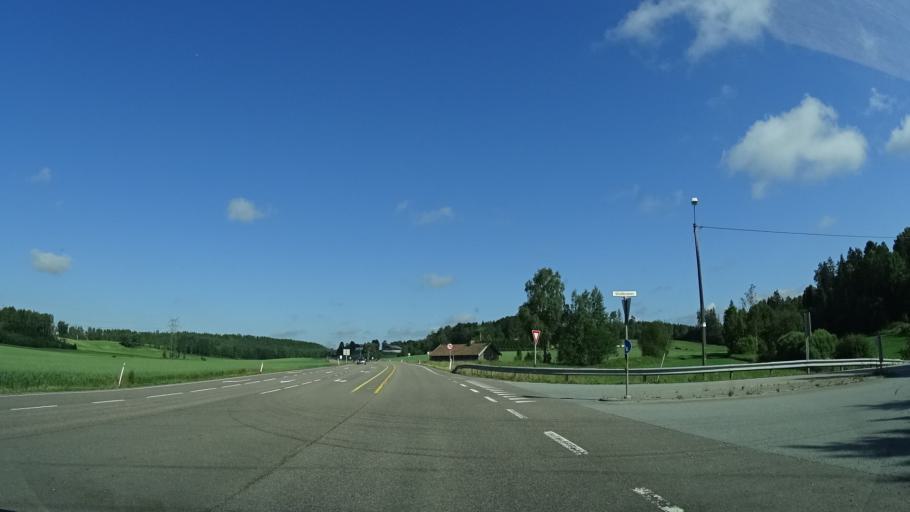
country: NO
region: Ostfold
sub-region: Hobol
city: Elvestad
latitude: 59.6546
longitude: 10.9192
